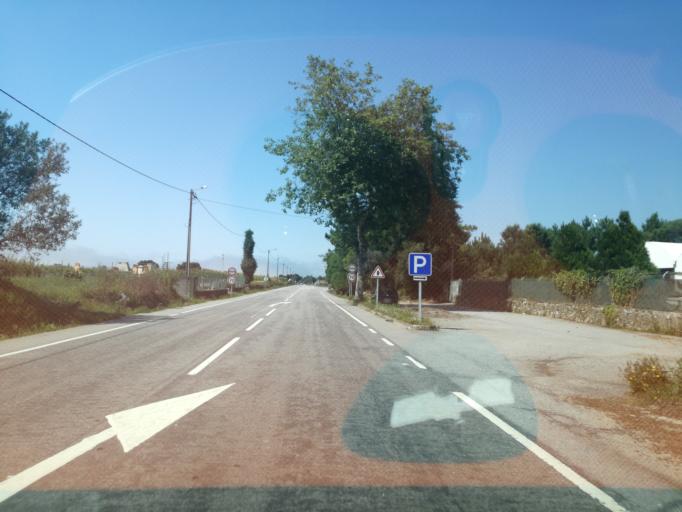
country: PT
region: Braga
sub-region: Esposende
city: Apulia
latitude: 41.4974
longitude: -8.7575
